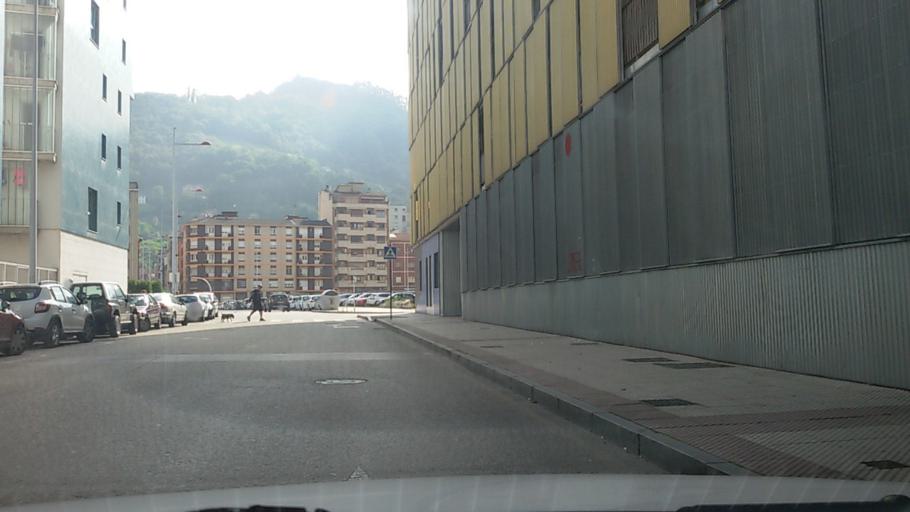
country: ES
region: Asturias
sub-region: Province of Asturias
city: Mieres
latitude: 43.2496
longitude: -5.7784
